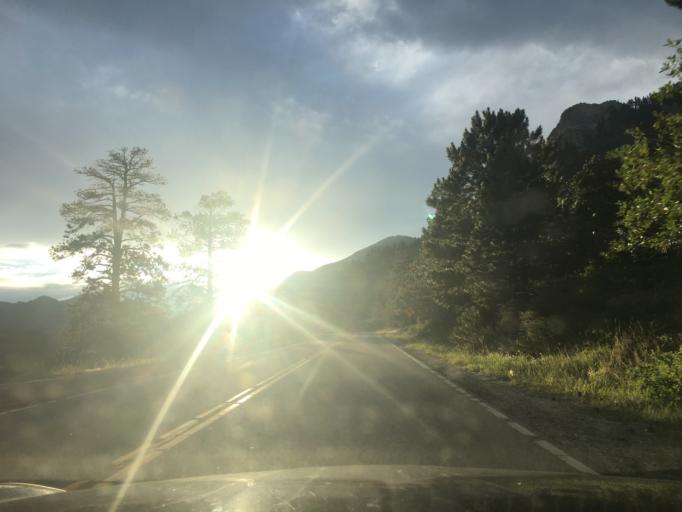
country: US
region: Colorado
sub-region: Larimer County
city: Estes Park
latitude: 40.3999
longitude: -105.5755
